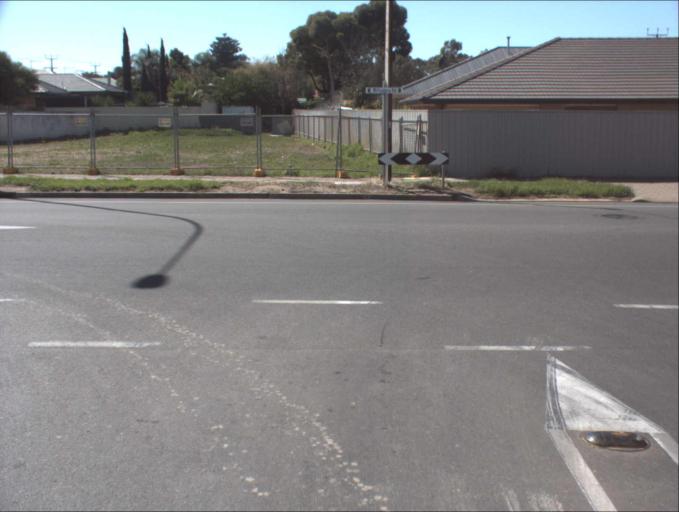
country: AU
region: South Australia
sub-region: Port Adelaide Enfield
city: Klemzig
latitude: -34.8650
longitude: 138.6365
